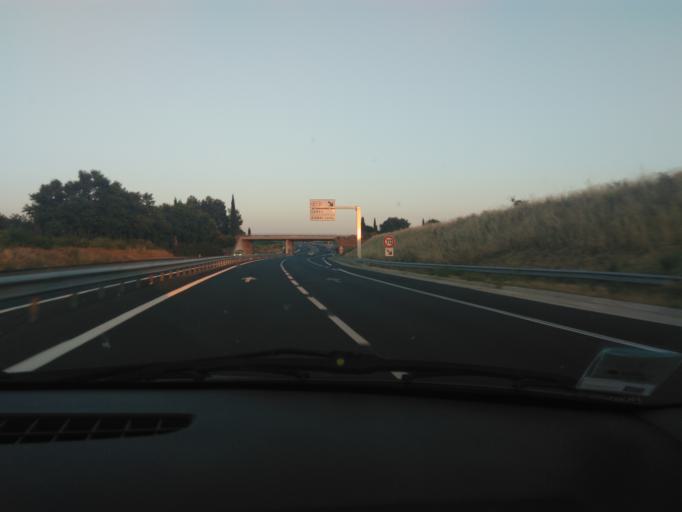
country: FR
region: Languedoc-Roussillon
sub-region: Departement de l'Herault
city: Gignac
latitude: 43.6496
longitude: 3.5436
